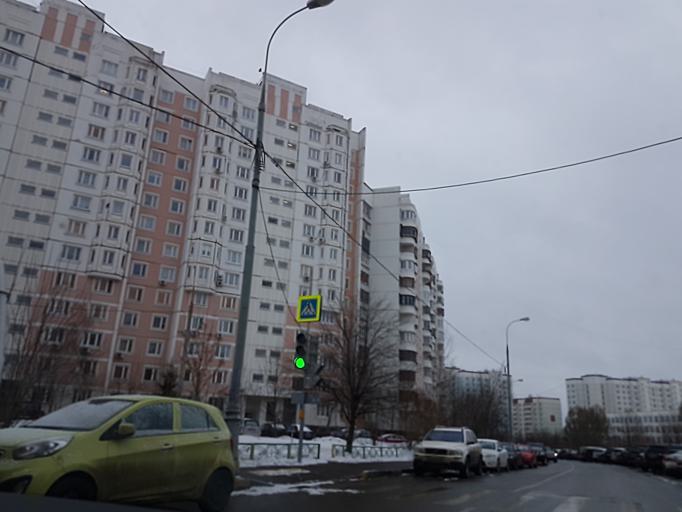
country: RU
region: Moskovskaya
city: Pavshino
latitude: 55.8306
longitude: 37.3504
